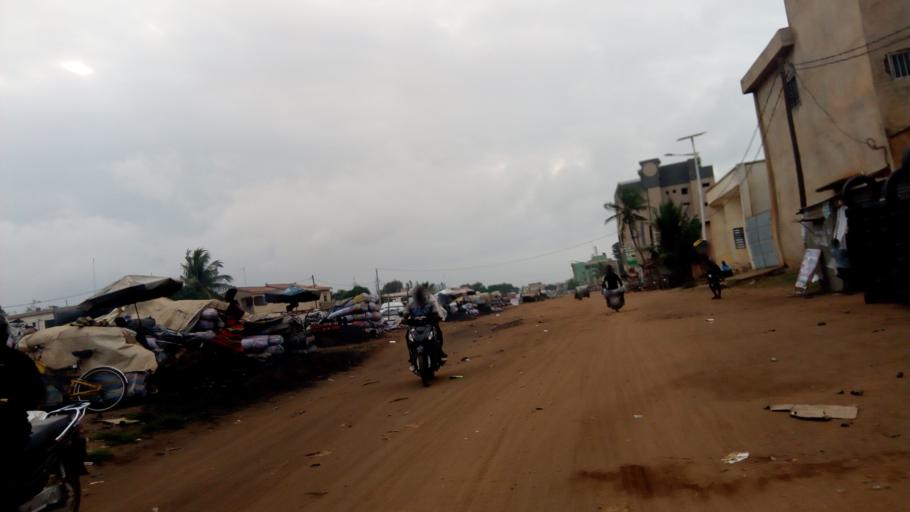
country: TG
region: Maritime
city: Lome
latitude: 6.1646
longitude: 1.2051
